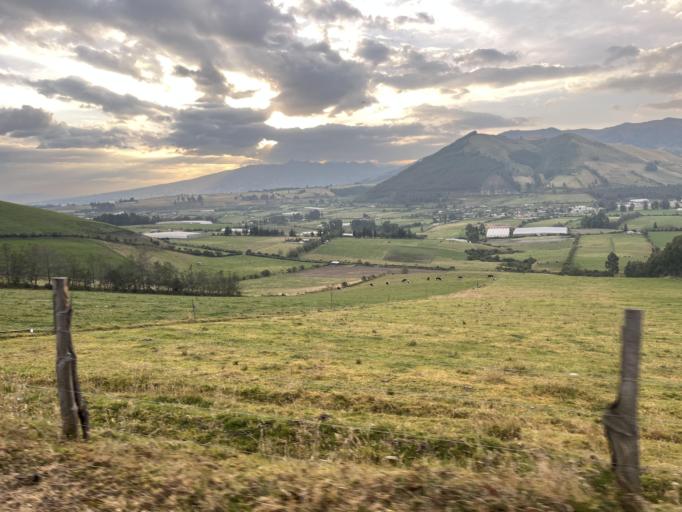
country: EC
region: Pichincha
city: Cayambe
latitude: 0.1010
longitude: -78.0866
